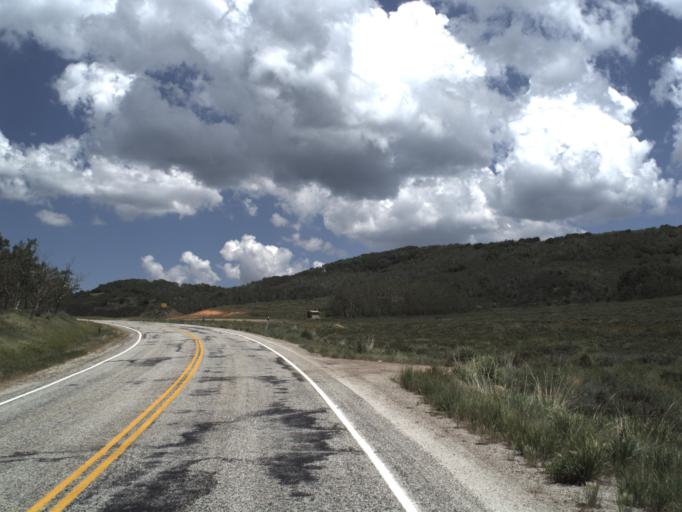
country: US
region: Utah
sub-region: Weber County
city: Wolf Creek
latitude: 41.4077
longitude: -111.5912
